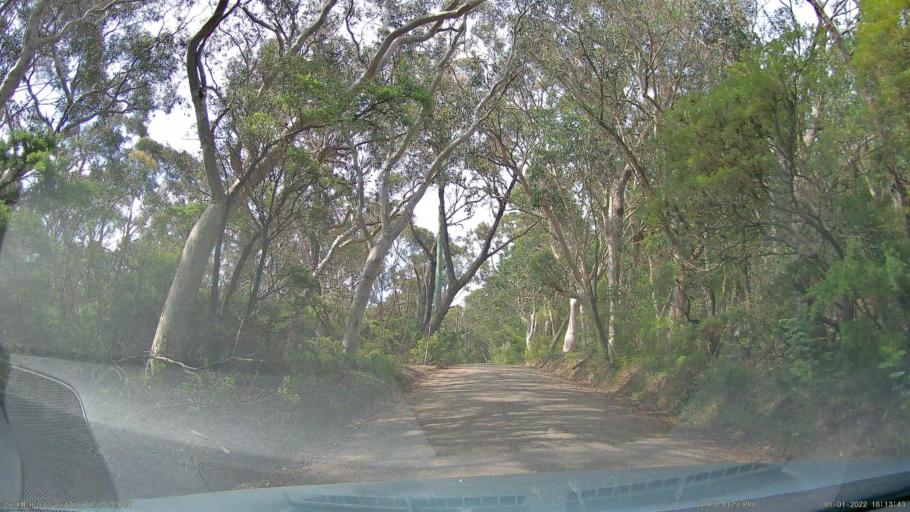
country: AU
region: New South Wales
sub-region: Blue Mountains Municipality
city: Blackheath
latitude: -33.6546
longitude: 150.2497
